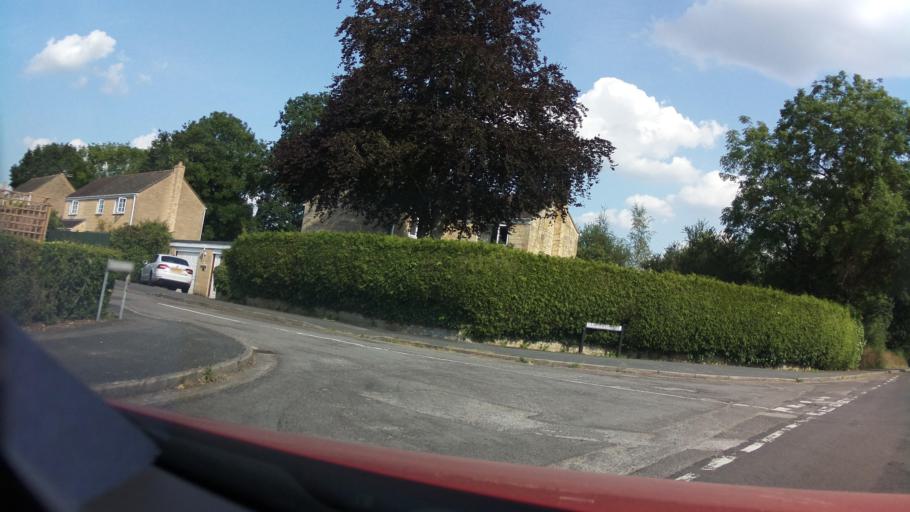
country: GB
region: England
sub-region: Wiltshire
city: Minety
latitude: 51.6167
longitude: -1.9662
